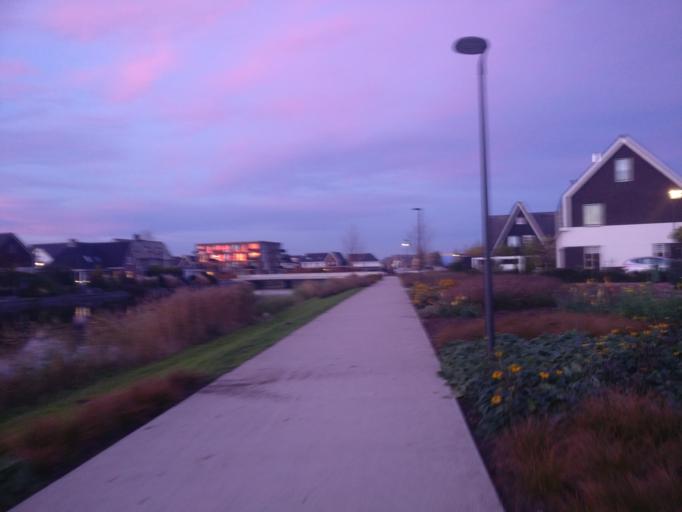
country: NL
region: North Holland
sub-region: Gemeente Huizen
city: Huizen
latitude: 52.2915
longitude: 5.2758
